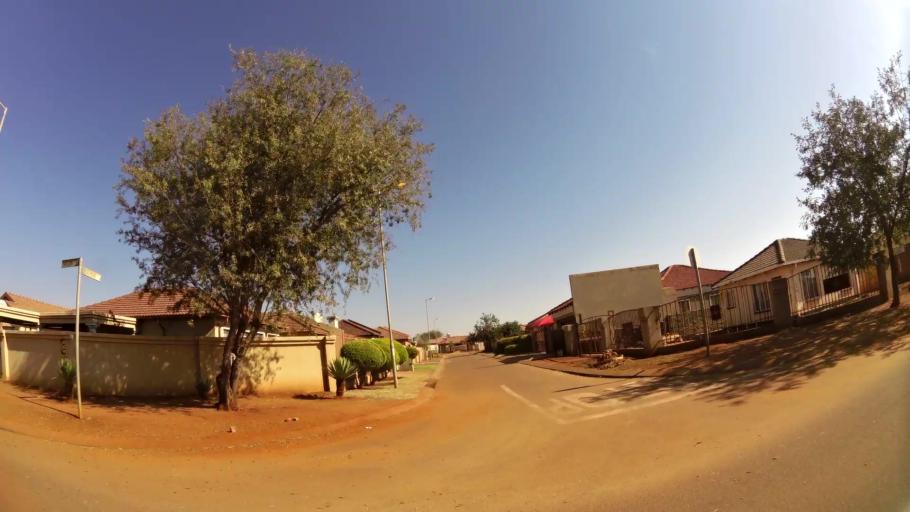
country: ZA
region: North-West
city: Ga-Rankuwa
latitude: -25.6368
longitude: 28.0817
